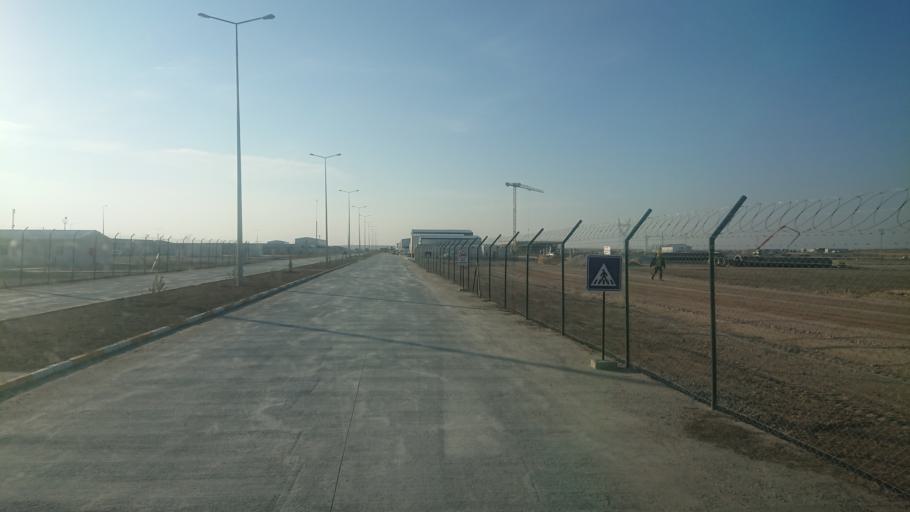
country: TR
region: Aksaray
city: Sultanhani
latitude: 38.1481
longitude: 33.5925
